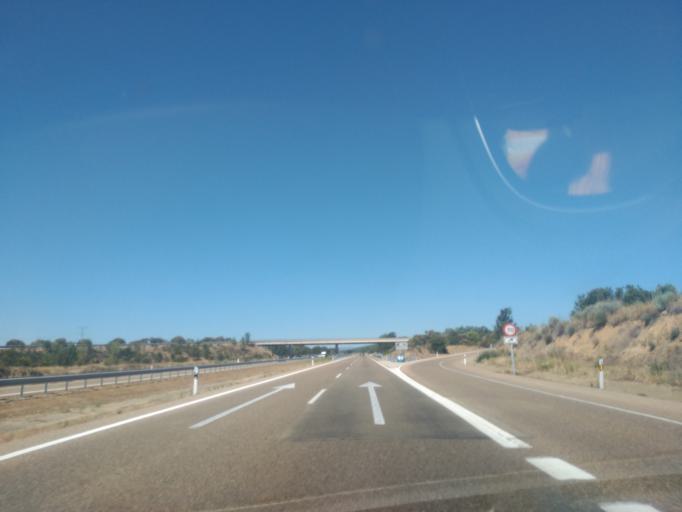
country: ES
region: Castille and Leon
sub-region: Provincia de Zamora
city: Mombuey
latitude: 42.0157
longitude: -6.3071
